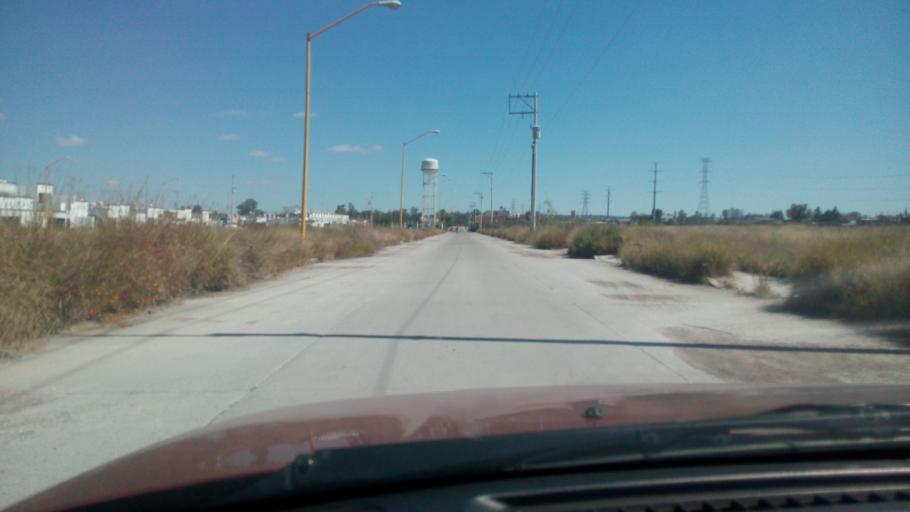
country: MX
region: Aguascalientes
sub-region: Aguascalientes
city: San Sebastian [Fraccionamiento]
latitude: 21.8367
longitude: -102.2992
